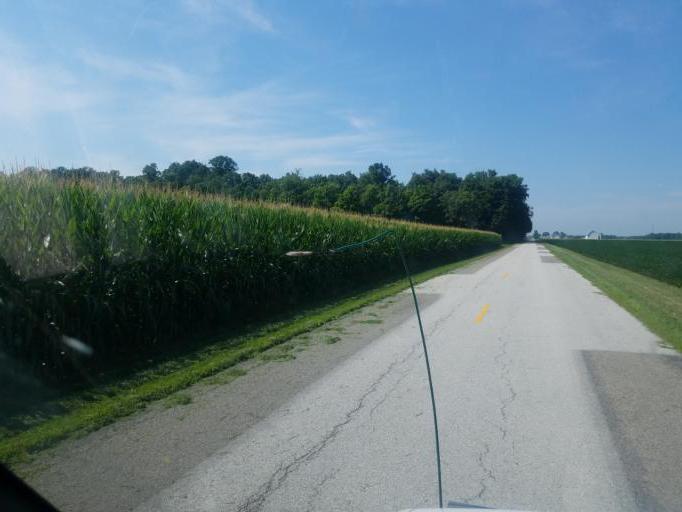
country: US
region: Ohio
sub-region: Shelby County
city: Jackson Center
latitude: 40.5217
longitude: -84.0119
